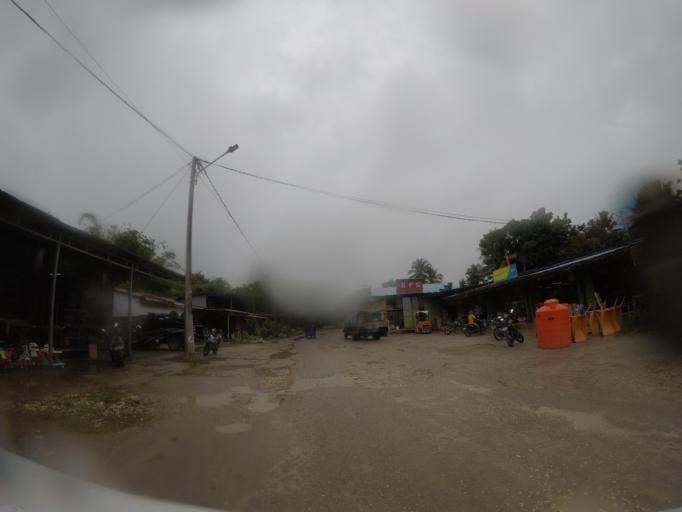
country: TL
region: Lautem
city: Lospalos
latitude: -8.5177
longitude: 126.9994
